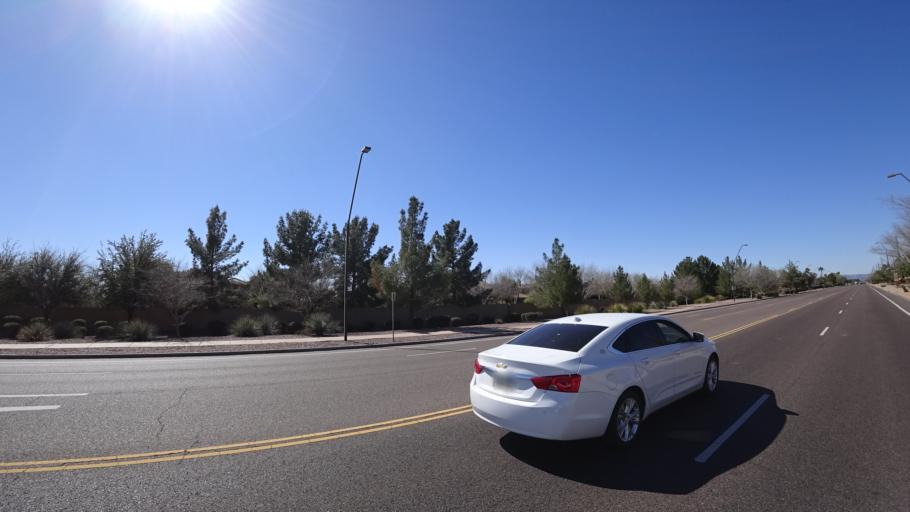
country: US
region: Arizona
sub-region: Maricopa County
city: Gilbert
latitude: 33.3499
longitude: -111.8134
